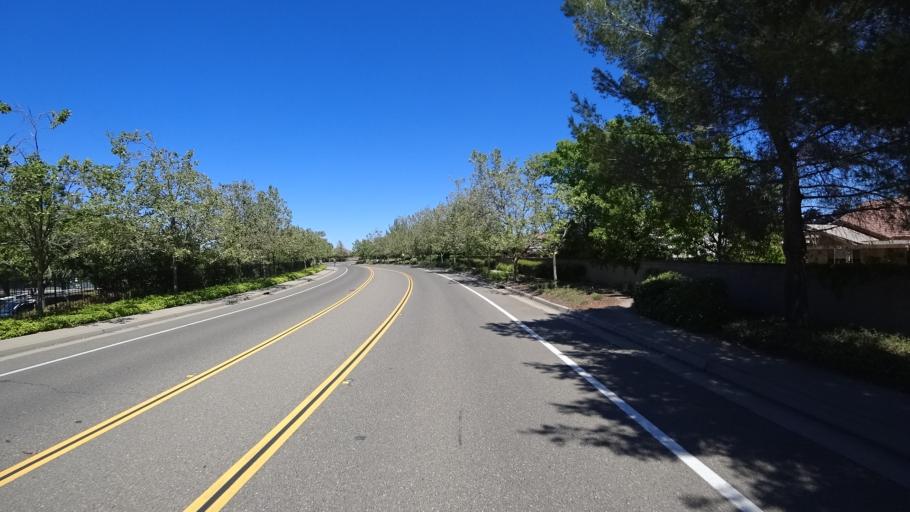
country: US
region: California
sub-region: Placer County
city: Rocklin
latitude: 38.8194
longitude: -121.2374
